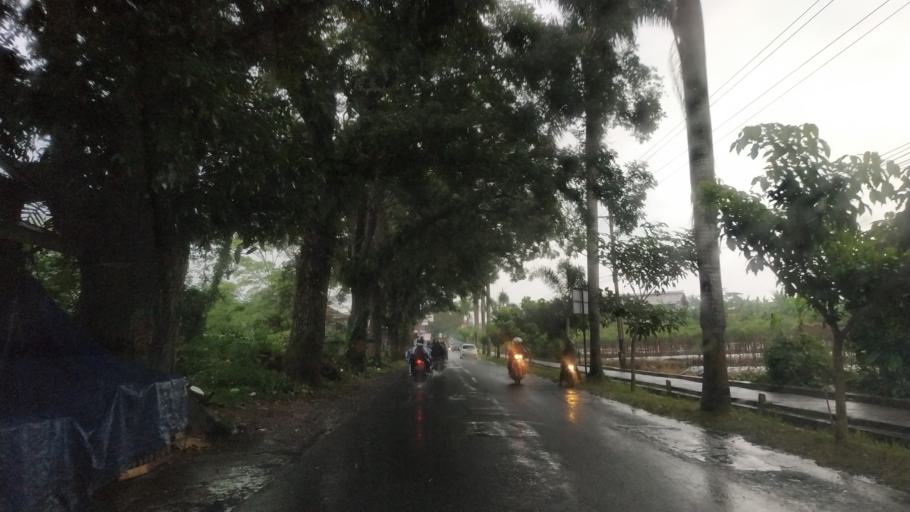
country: ID
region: Central Java
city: Magelang
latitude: -7.3148
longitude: 110.1681
